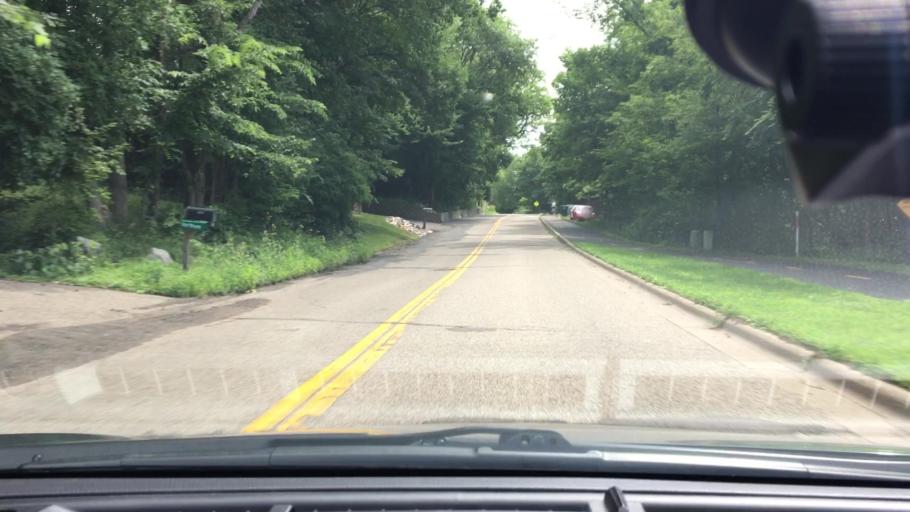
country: US
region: Minnesota
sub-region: Hennepin County
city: New Hope
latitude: 45.0142
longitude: -93.4166
